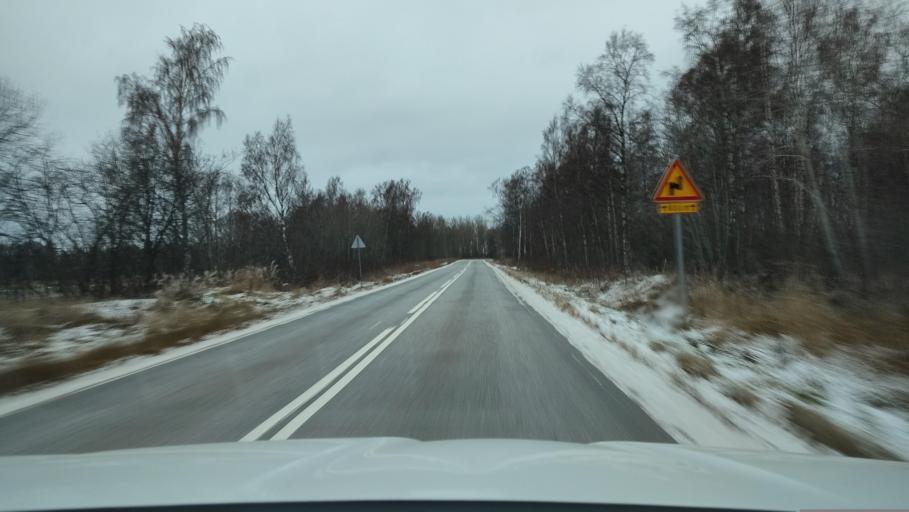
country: FI
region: Ostrobothnia
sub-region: Vaasa
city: Replot
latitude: 63.2838
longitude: 21.3351
